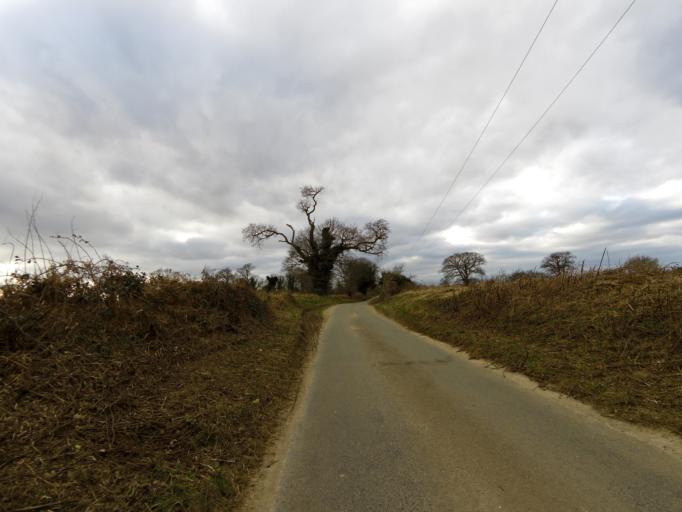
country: GB
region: England
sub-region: Suffolk
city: Woodbridge
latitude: 52.0445
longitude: 1.3233
